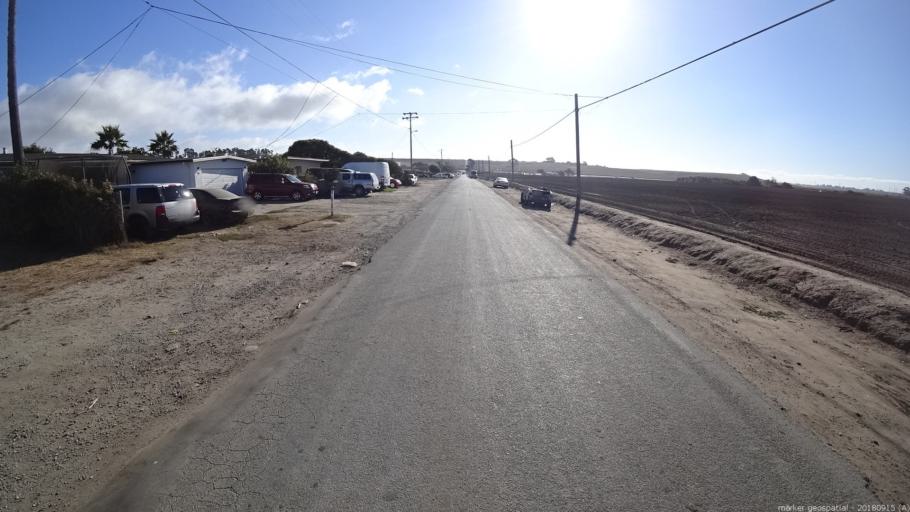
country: US
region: California
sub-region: Monterey County
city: Elkhorn
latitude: 36.8309
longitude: -121.7780
